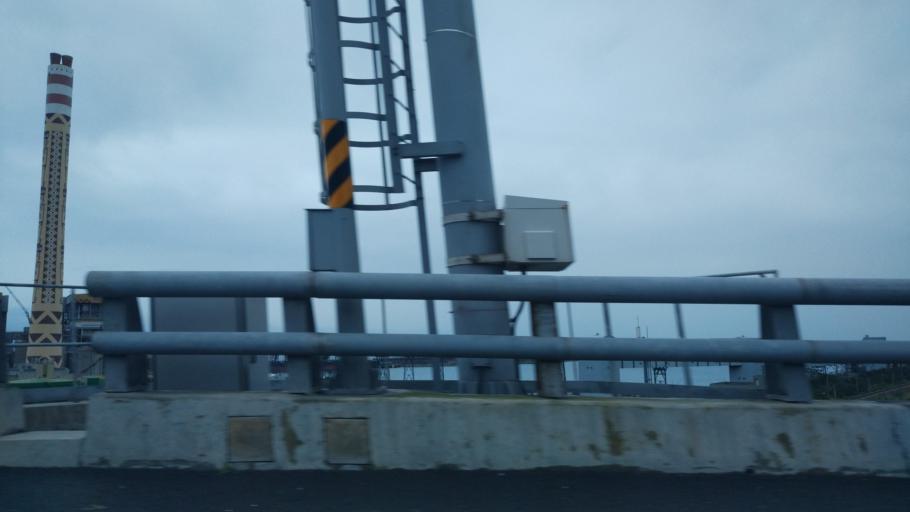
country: TW
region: Taiwan
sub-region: Hualien
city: Hualian
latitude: 24.3109
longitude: 121.7591
